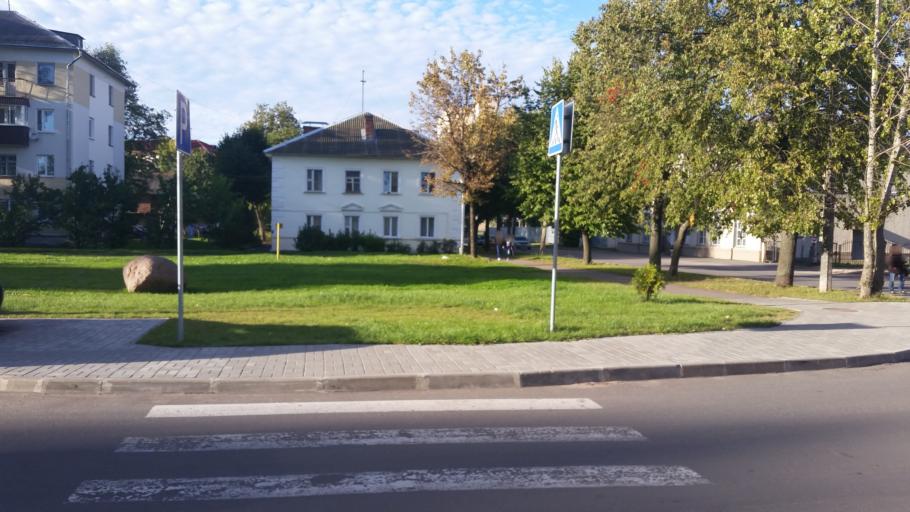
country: BY
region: Vitebsk
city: Vitebsk
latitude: 55.1832
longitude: 30.1911
